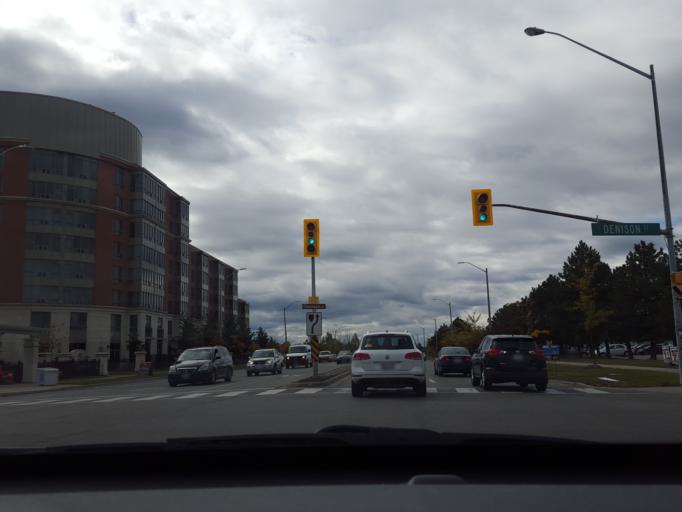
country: CA
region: Ontario
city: Markham
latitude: 43.8346
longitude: -79.3043
